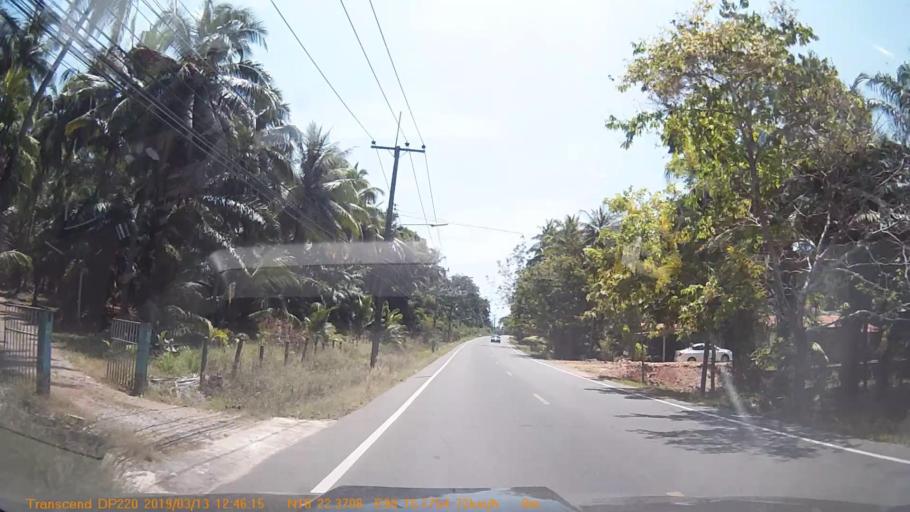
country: TH
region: Chumphon
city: Chumphon
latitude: 10.3723
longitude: 99.2629
